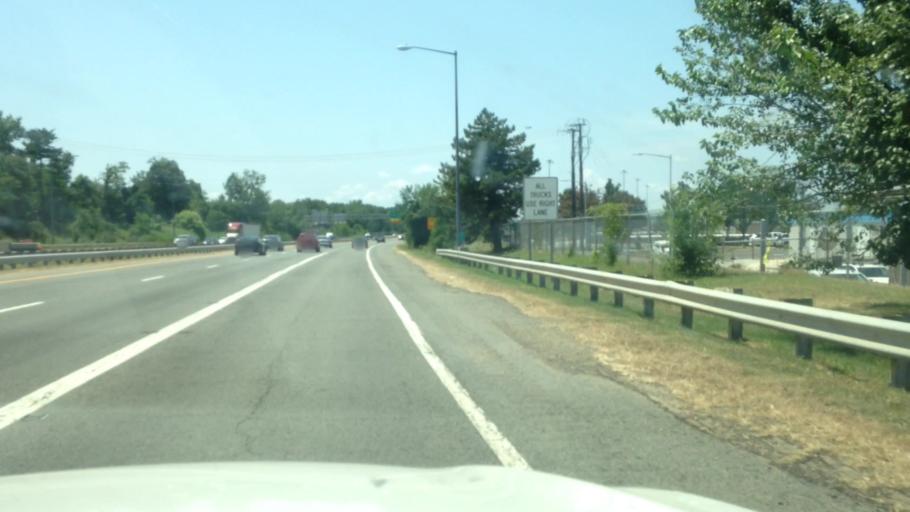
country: US
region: Maryland
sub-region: Prince George's County
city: Glassmanor
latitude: 38.8187
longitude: -77.0179
